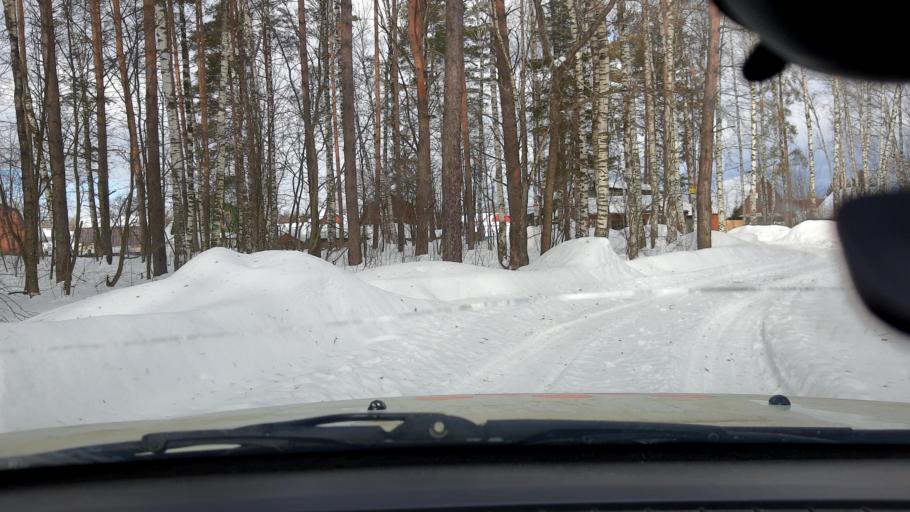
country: RU
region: Nizjnij Novgorod
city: Neklyudovo
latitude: 56.4493
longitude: 43.9815
